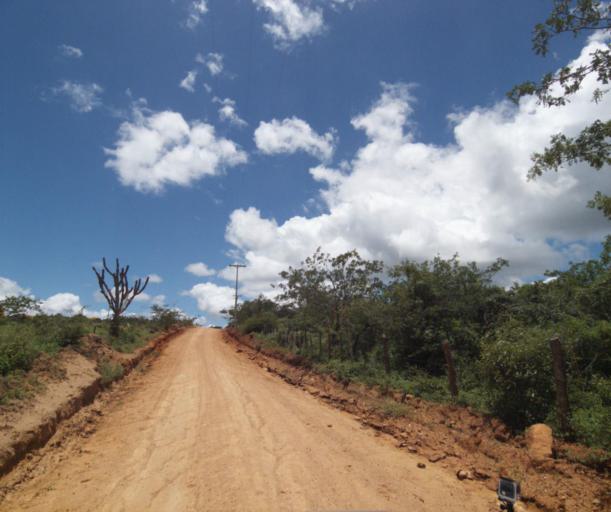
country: BR
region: Bahia
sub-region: Pocoes
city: Pocoes
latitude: -14.3793
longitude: -40.3943
